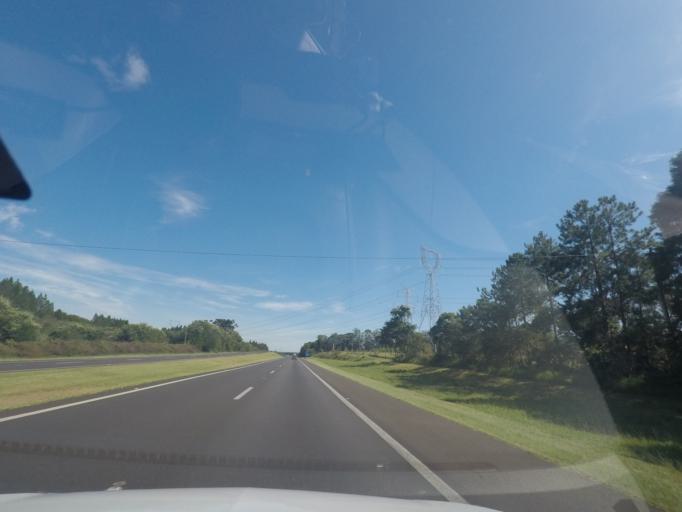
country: BR
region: Sao Paulo
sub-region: Itirapina
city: Itirapina
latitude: -22.1590
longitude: -47.7917
